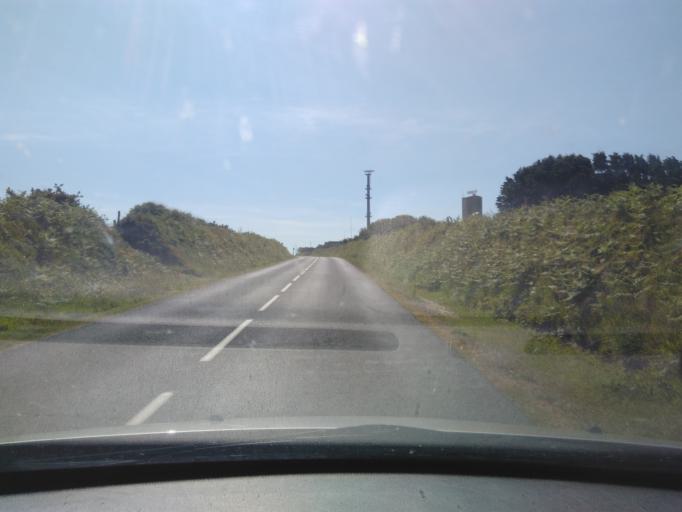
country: FR
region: Lower Normandy
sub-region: Departement de la Manche
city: Beaumont-Hague
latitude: 49.6861
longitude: -1.9099
